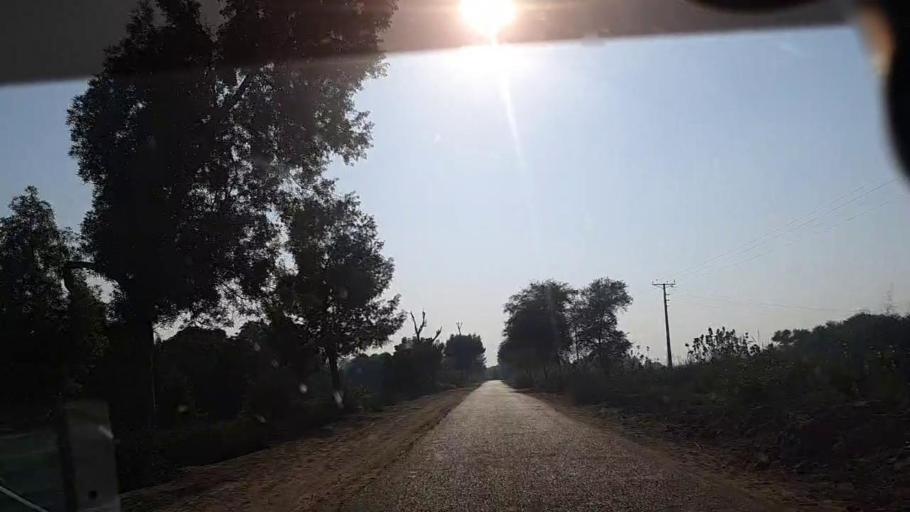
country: PK
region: Sindh
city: Sobhadero
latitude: 27.2374
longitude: 68.2802
